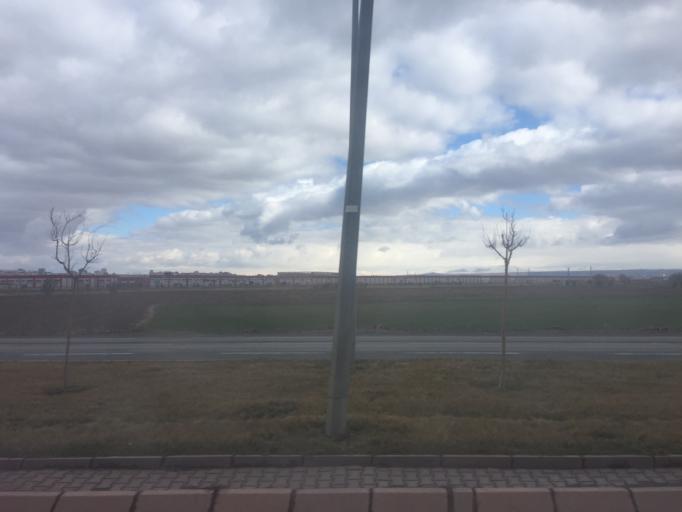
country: TR
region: Kayseri
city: Melikgazi
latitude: 38.7775
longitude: 35.4121
